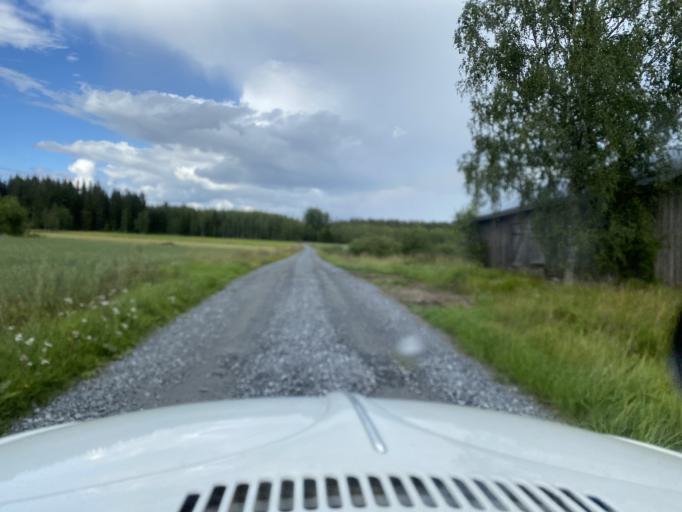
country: FI
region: Pirkanmaa
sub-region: Lounais-Pirkanmaa
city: Punkalaidun
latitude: 61.1322
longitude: 23.0666
